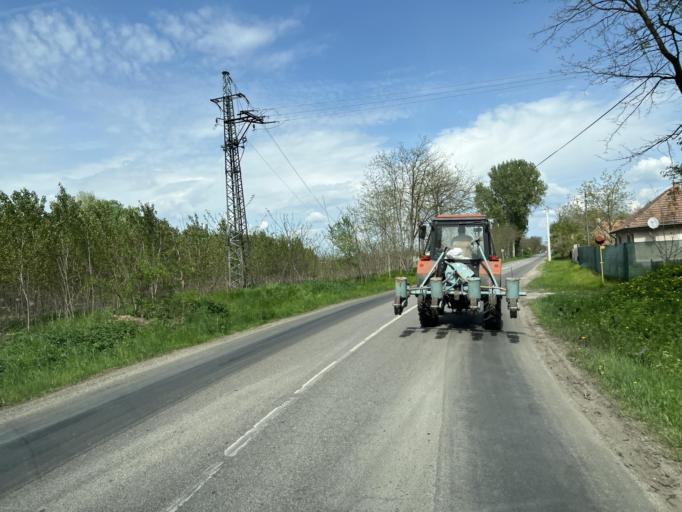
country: HU
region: Pest
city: Albertirsa
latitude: 47.2234
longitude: 19.6101
